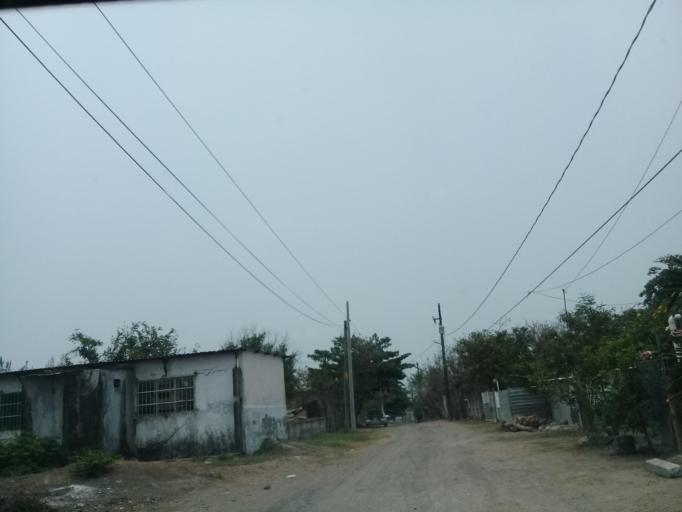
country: MX
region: Veracruz
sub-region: Veracruz
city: Las Amapolas
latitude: 19.1492
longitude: -96.2017
